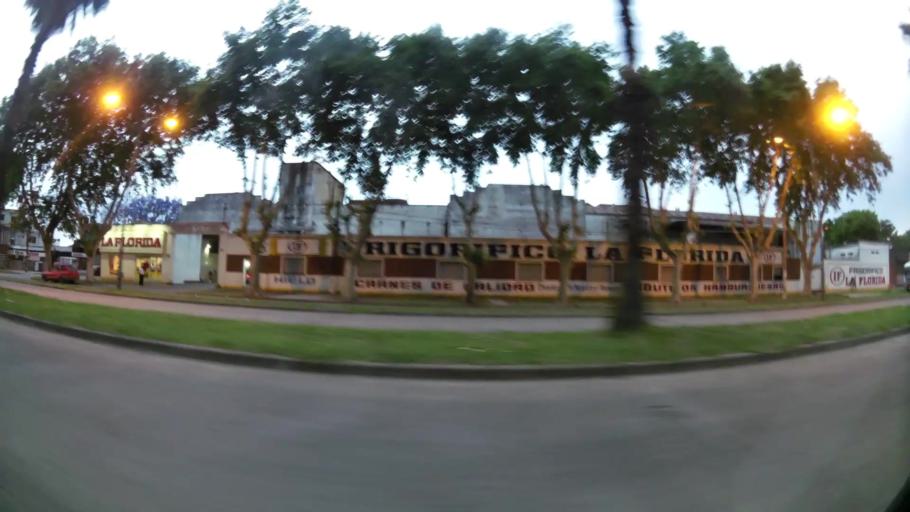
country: AR
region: Santa Fe
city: Granadero Baigorria
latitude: -32.8799
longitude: -60.6967
